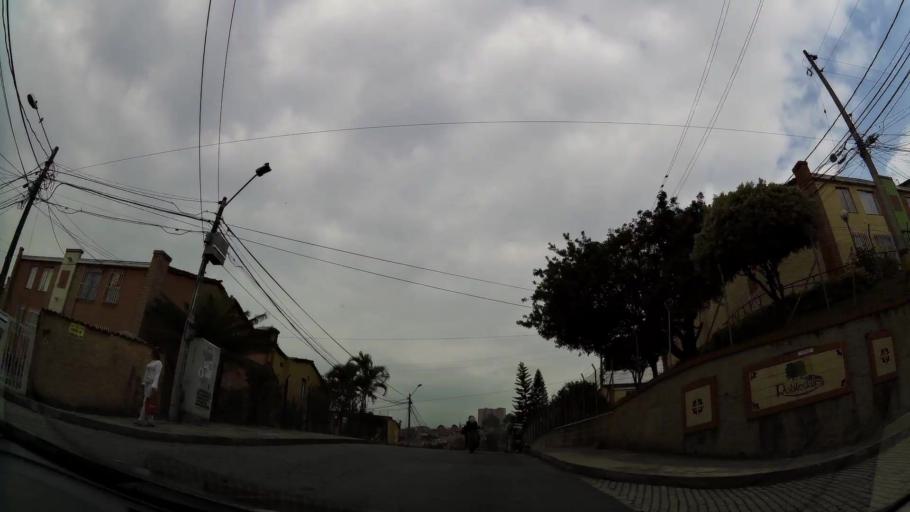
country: CO
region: Antioquia
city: Medellin
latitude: 6.2841
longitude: -75.5967
